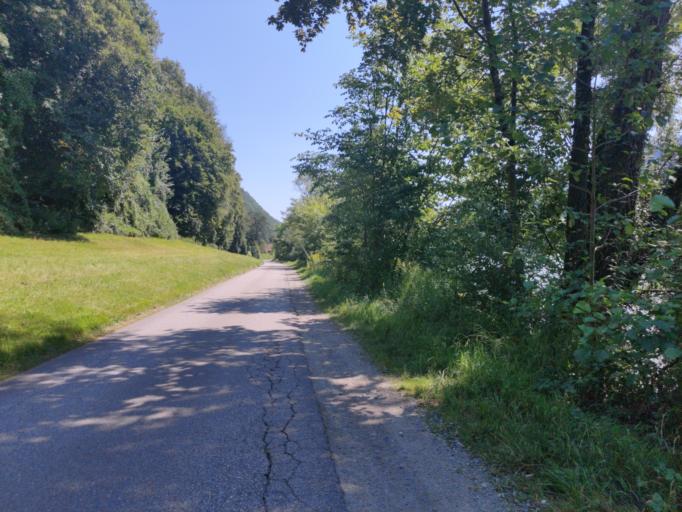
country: AT
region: Upper Austria
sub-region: Politischer Bezirk Rohrbach
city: Pfarrkirchen im Muehlkreis
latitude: 48.4575
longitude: 13.8183
